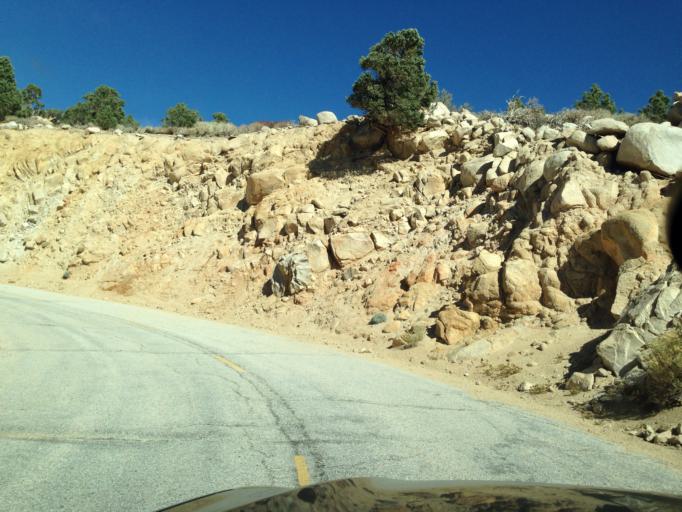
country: US
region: California
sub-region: Inyo County
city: Lone Pine
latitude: 36.4813
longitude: -118.1014
